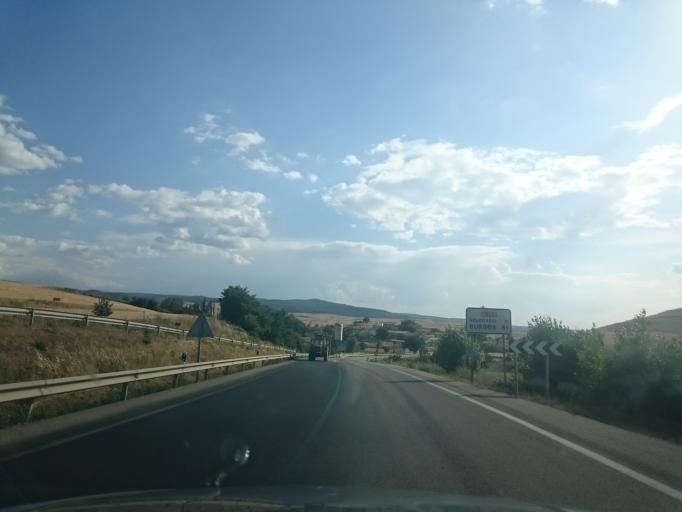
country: ES
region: Castille and Leon
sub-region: Provincia de Burgos
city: Fresnena
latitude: 42.4304
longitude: -3.1314
